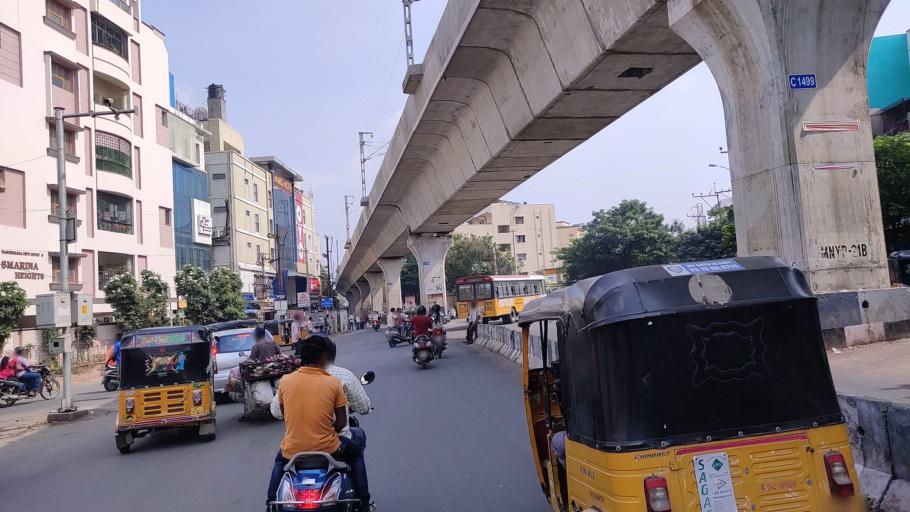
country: IN
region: Telangana
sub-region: Rangareddi
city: Kukatpalli
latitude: 17.4366
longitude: 78.4330
